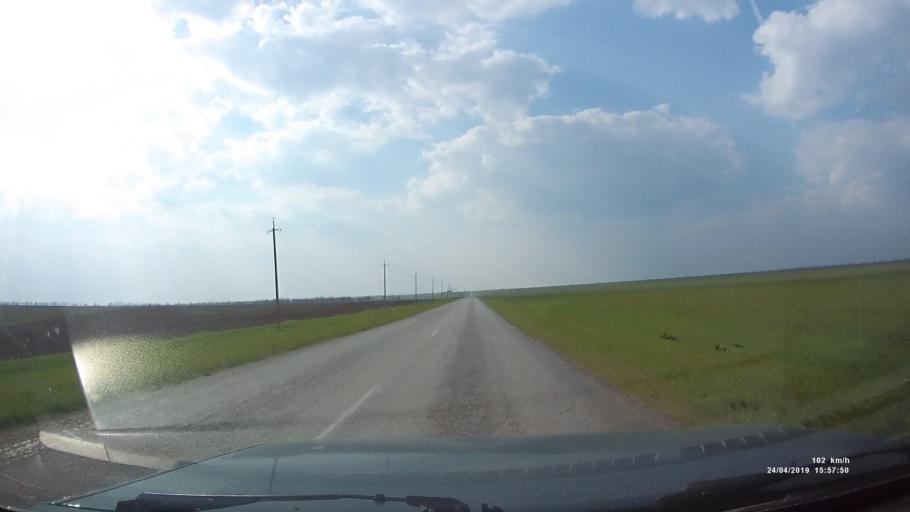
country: RU
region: Kalmykiya
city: Yashalta
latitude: 46.6086
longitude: 42.5013
